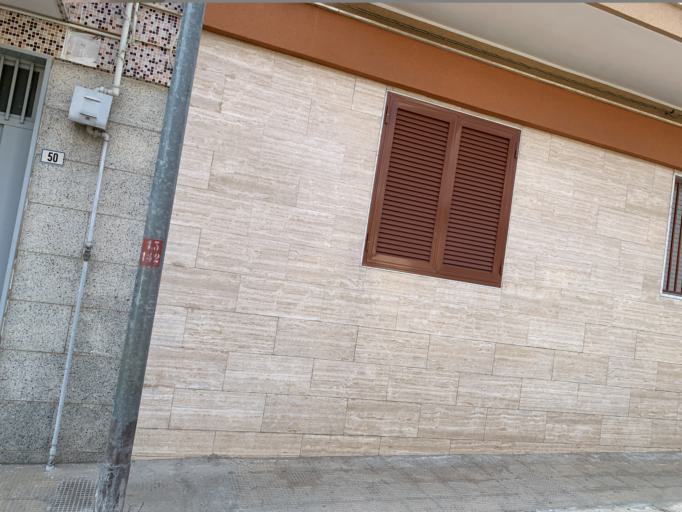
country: IT
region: Apulia
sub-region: Provincia di Barletta - Andria - Trani
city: Andria
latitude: 41.2319
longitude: 16.2857
